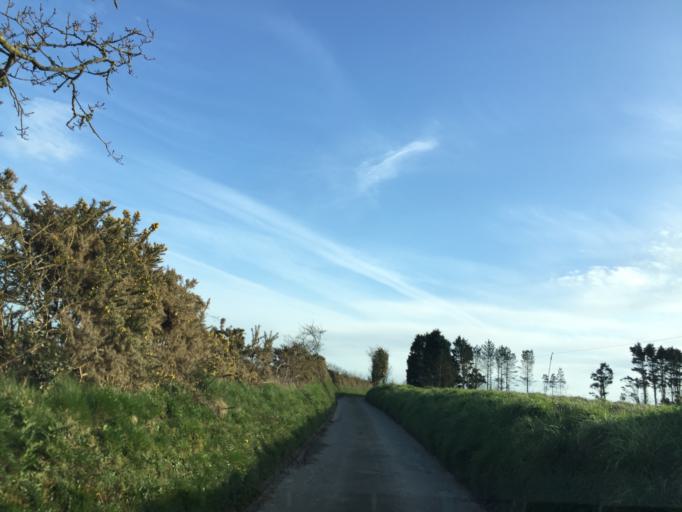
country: JE
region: St Helier
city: Saint Helier
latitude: 49.2466
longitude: -2.0983
